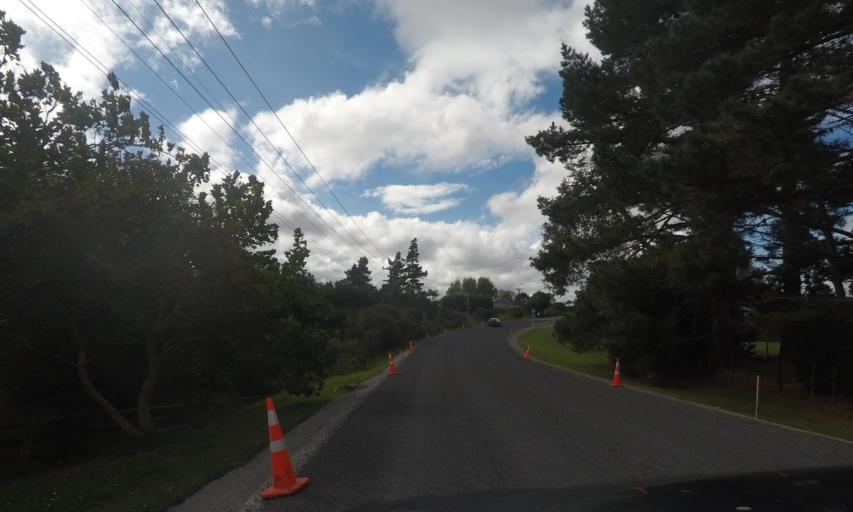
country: NZ
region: Auckland
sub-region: Auckland
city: Rosebank
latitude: -36.7907
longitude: 174.6371
